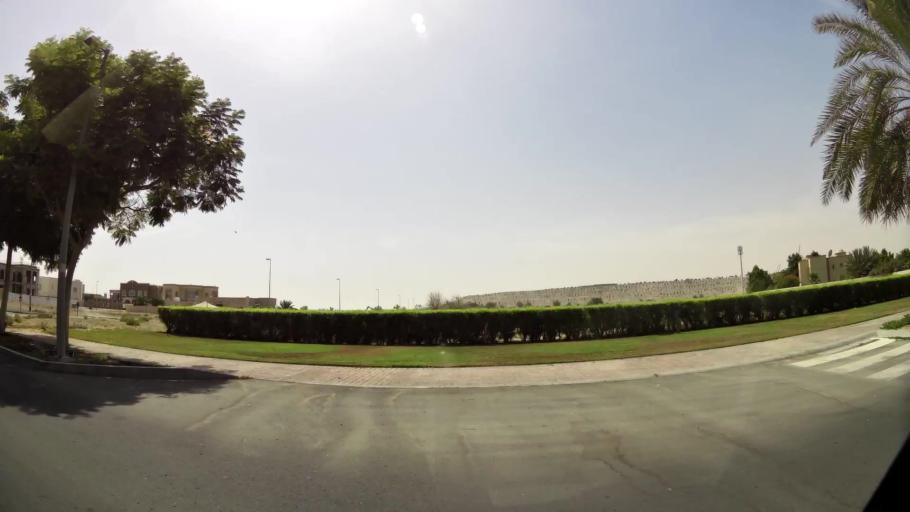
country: AE
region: Ash Shariqah
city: Sharjah
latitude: 25.1899
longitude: 55.4453
